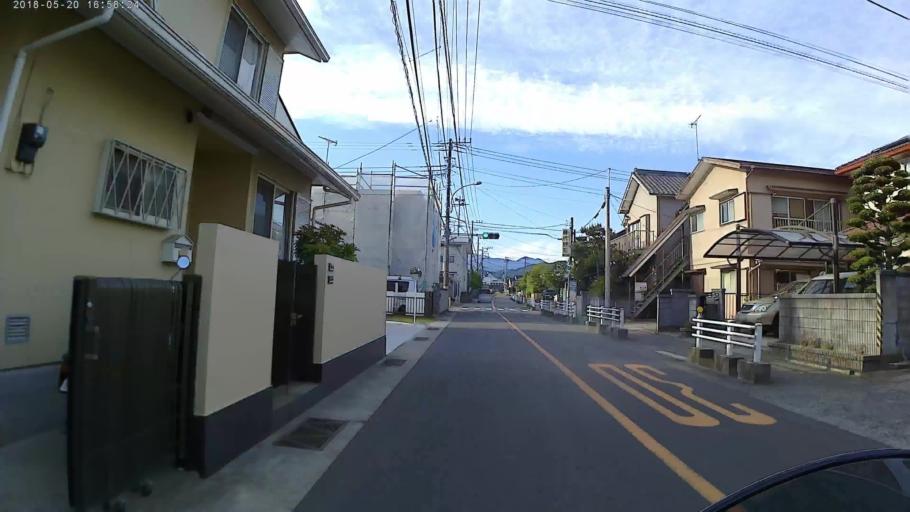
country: JP
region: Kanagawa
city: Odawara
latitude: 35.2826
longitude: 139.1776
